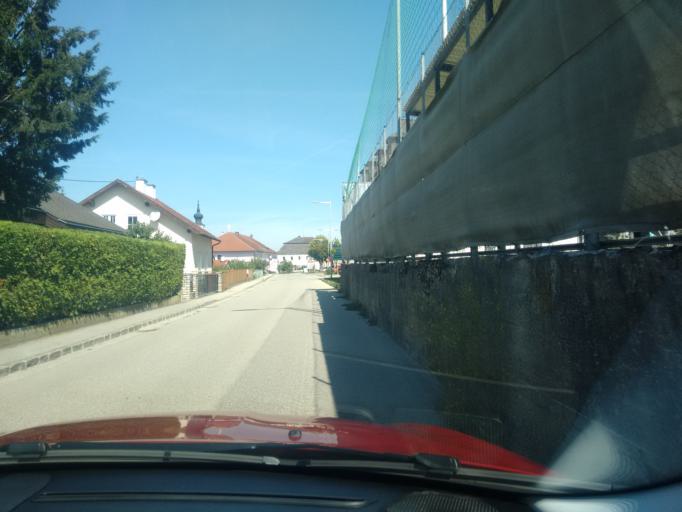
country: AT
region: Upper Austria
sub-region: Wels-Land
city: Steinhaus
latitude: 48.1140
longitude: 14.0215
